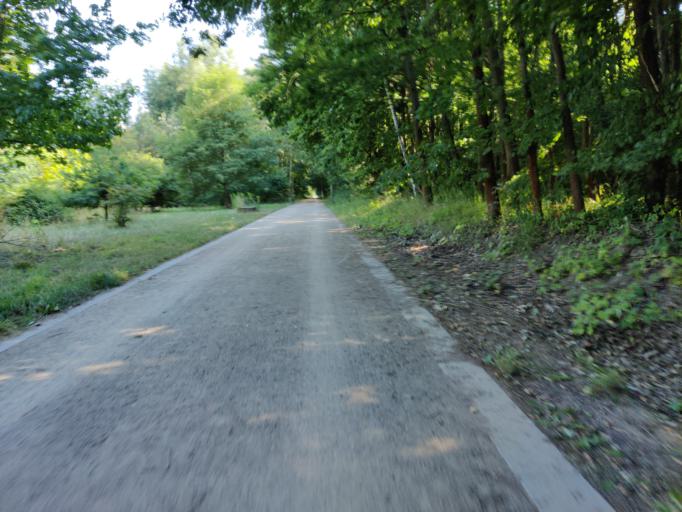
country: DE
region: Saxony
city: Markkleeberg
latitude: 51.2867
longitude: 12.3516
